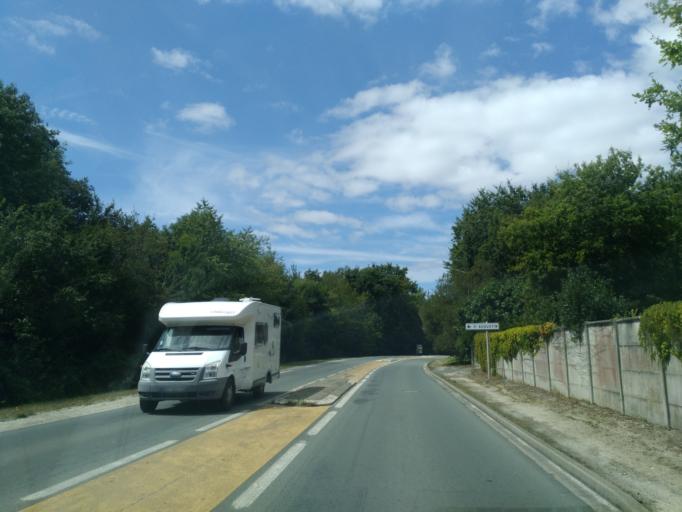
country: FR
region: Poitou-Charentes
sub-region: Departement de la Charente-Maritime
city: Breuillet
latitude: 45.6995
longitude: -1.0544
